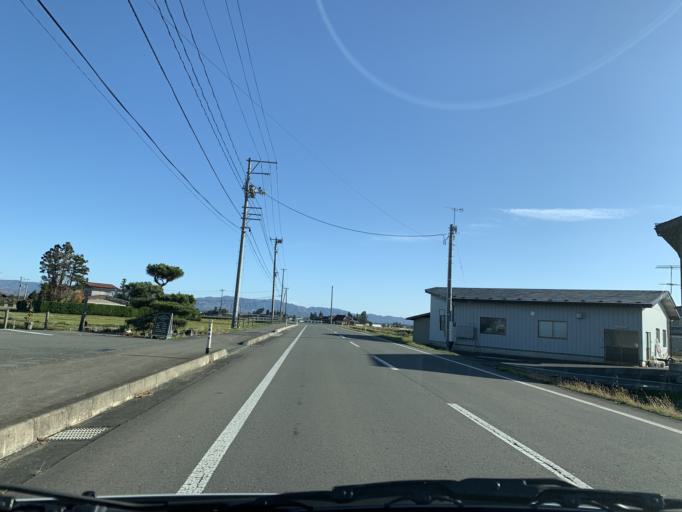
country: JP
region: Iwate
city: Mizusawa
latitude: 39.1634
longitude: 141.1045
